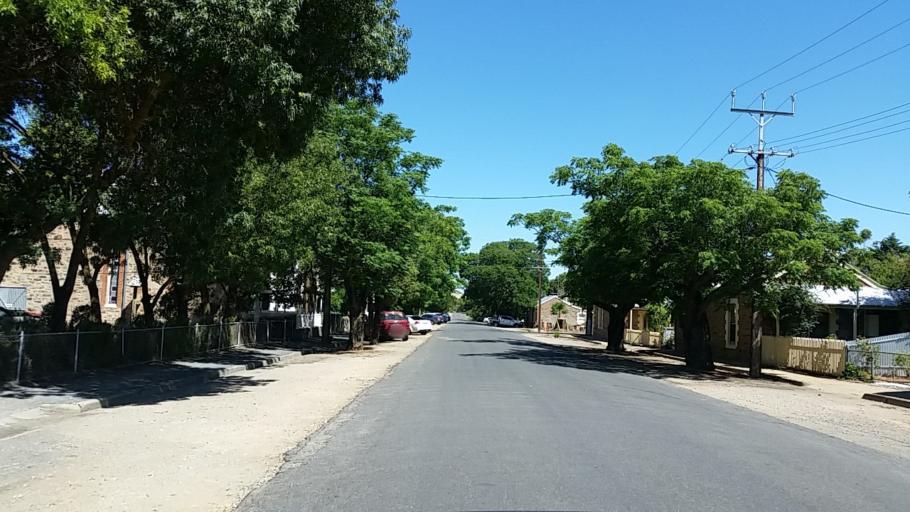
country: AU
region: South Australia
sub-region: Clare and Gilbert Valleys
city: Clare
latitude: -33.6826
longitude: 138.9398
